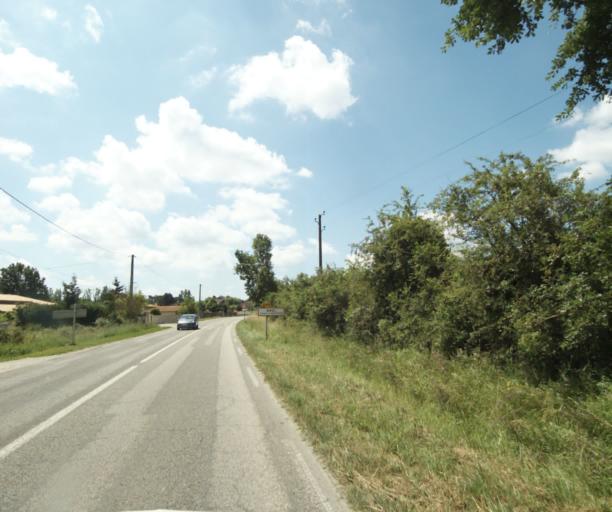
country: FR
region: Midi-Pyrenees
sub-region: Departement du Tarn-et-Garonne
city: Montauban
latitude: 44.0598
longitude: 1.3617
